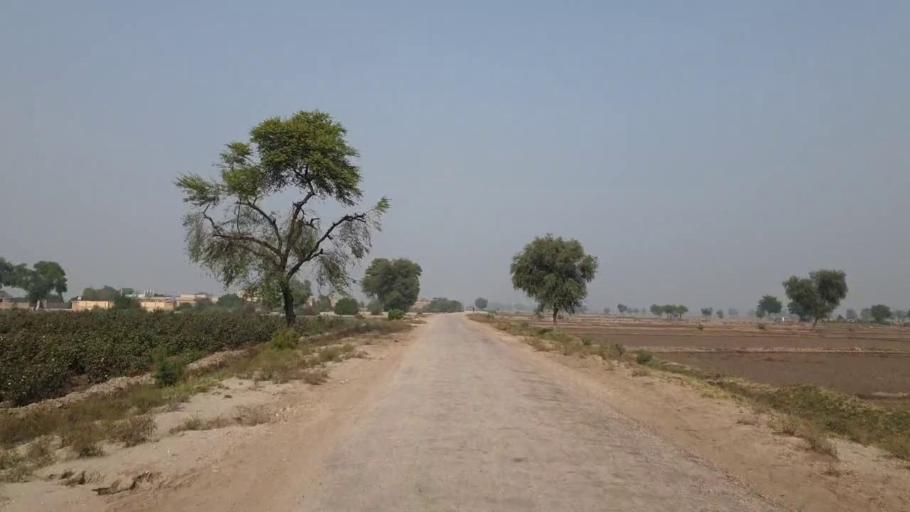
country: PK
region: Sindh
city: Bhan
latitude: 26.5122
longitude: 67.6895
